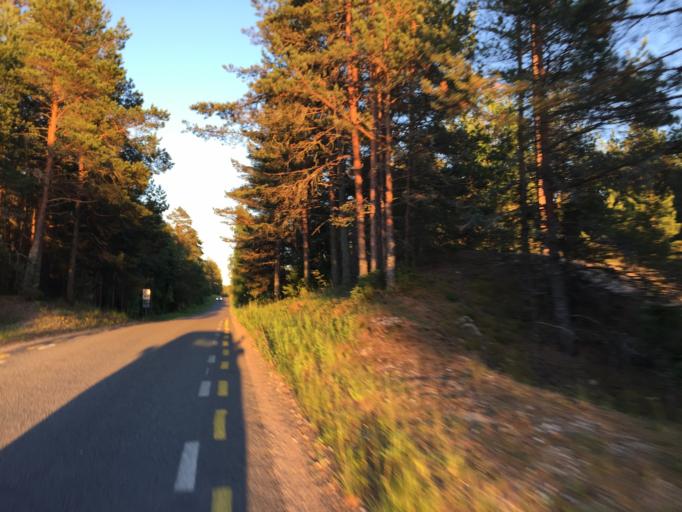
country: EE
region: Harju
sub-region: Raasiku vald
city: Raasiku
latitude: 59.5059
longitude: 25.2817
